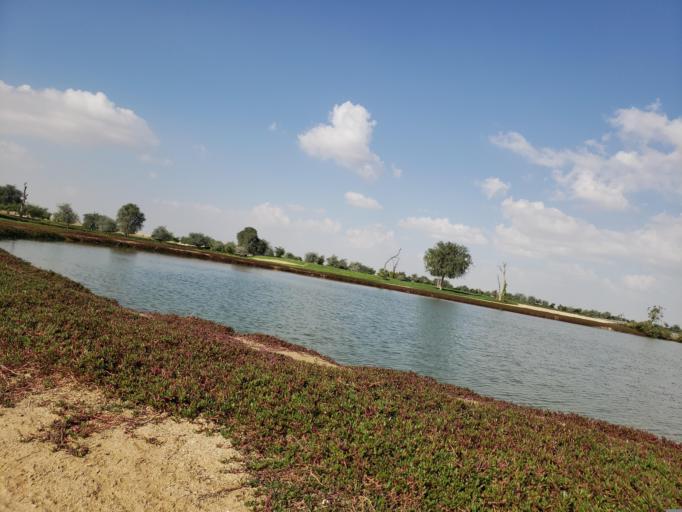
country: AE
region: Dubai
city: Dubai
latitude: 24.8526
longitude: 55.2477
